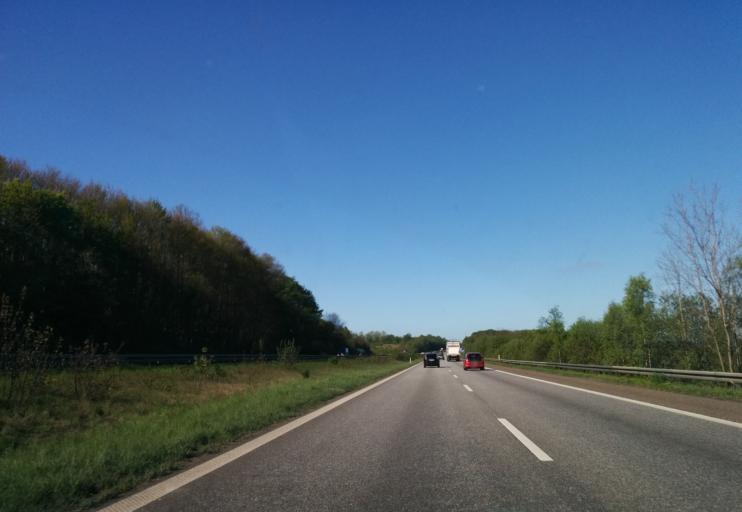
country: DK
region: Central Jutland
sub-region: Skanderborg Kommune
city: Skanderborg
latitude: 56.0545
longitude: 9.9461
